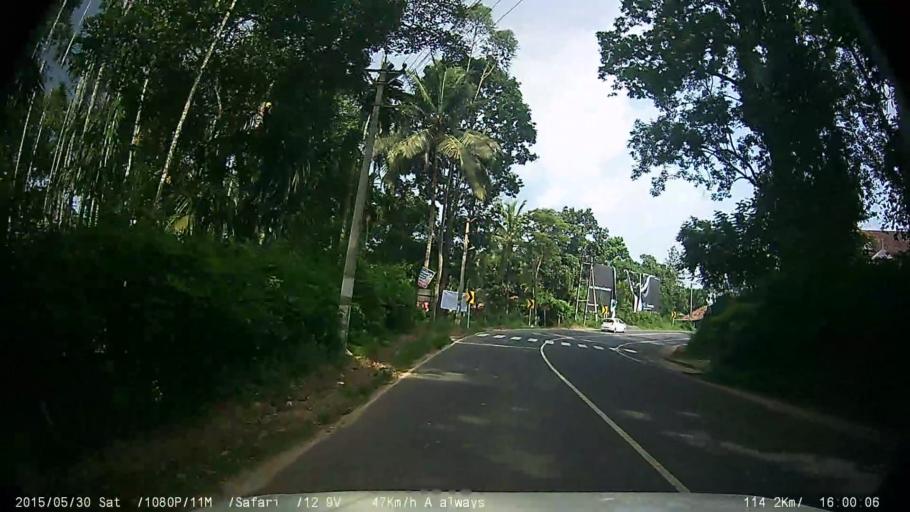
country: IN
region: Kerala
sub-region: Wayanad
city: Kalpetta
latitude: 11.6416
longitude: 76.0870
